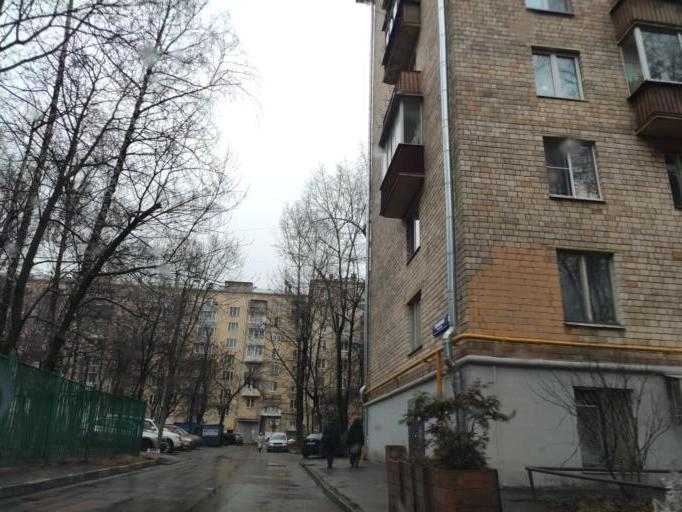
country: RU
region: Moskovskaya
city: Semenovskoye
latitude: 55.6773
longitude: 37.5260
